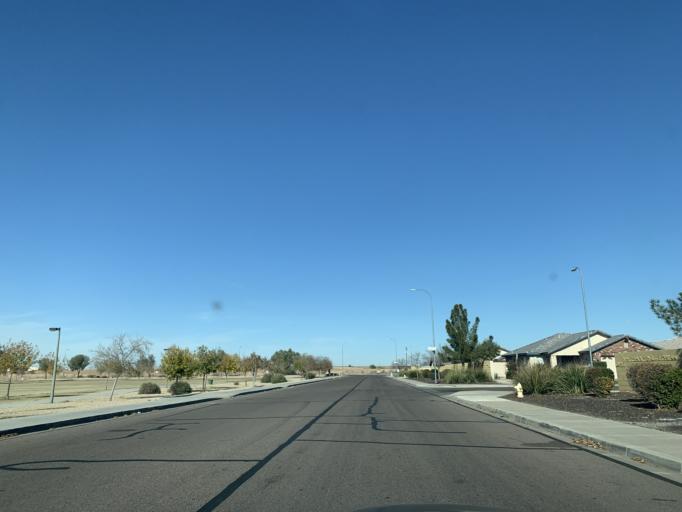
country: US
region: Arizona
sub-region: Maricopa County
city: Laveen
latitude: 33.3976
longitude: -112.1250
